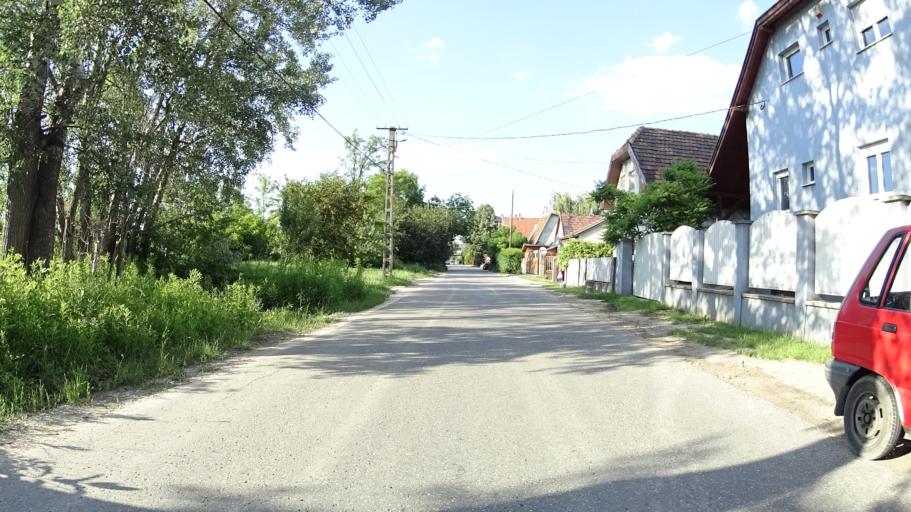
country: HU
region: Pest
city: Dunaharaszti
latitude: 47.3702
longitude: 19.0866
